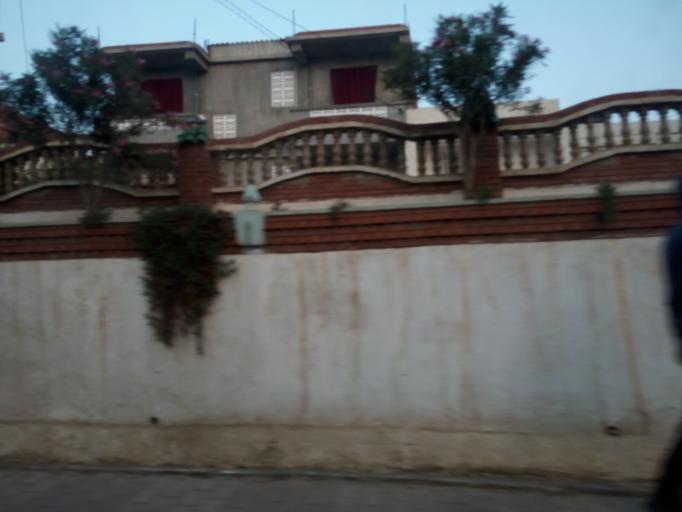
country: DZ
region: Tipaza
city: Bou Ismail
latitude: 36.6226
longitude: 2.6537
